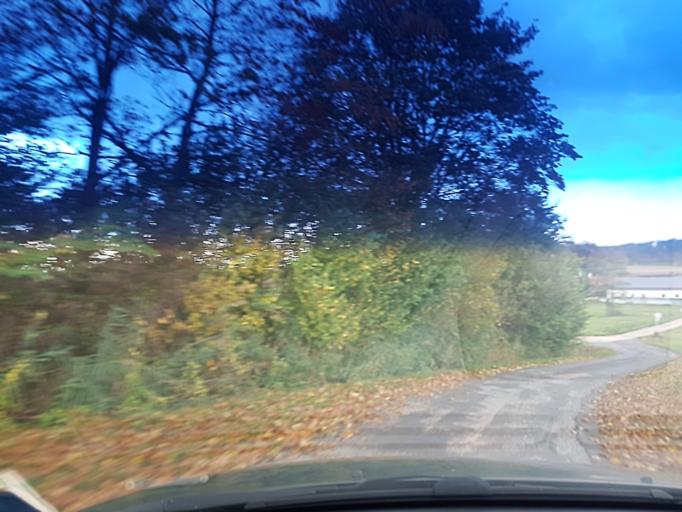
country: DE
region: Bavaria
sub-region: Regierungsbezirk Mittelfranken
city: Burghaslach
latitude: 49.7642
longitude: 10.5462
